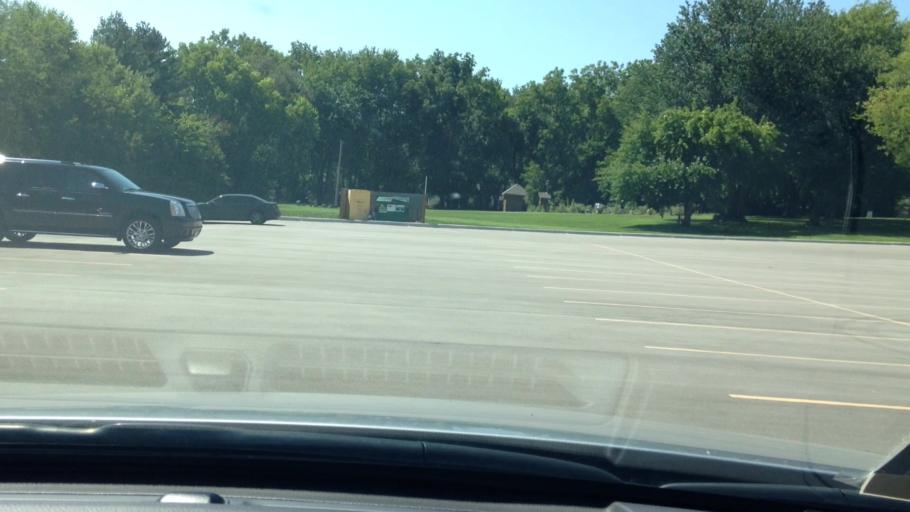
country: US
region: Kansas
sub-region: Johnson County
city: Overland Park
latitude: 38.9589
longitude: -94.6508
